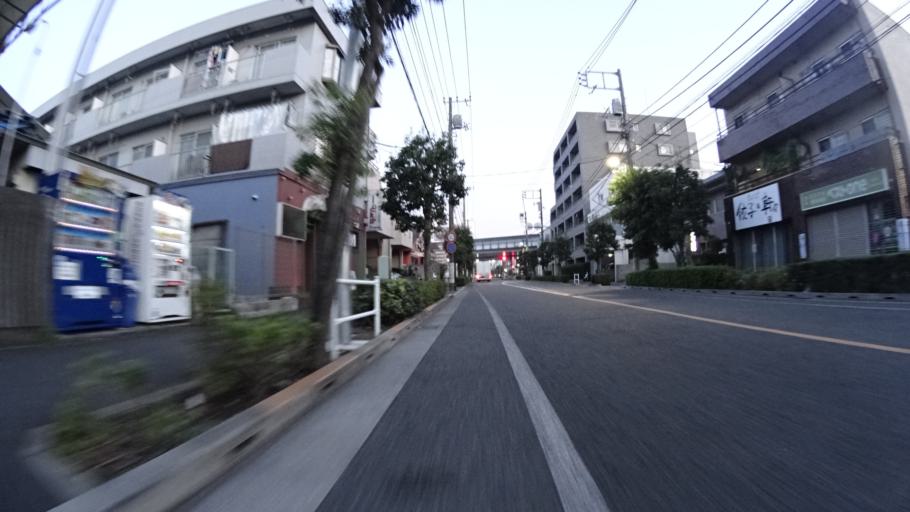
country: JP
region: Tokyo
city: Chofugaoka
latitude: 35.6563
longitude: 139.5266
